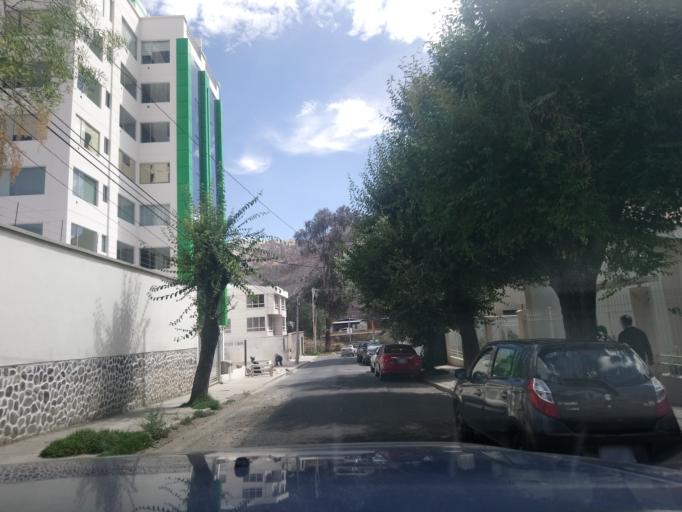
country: BO
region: La Paz
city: La Paz
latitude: -16.5268
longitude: -68.1106
